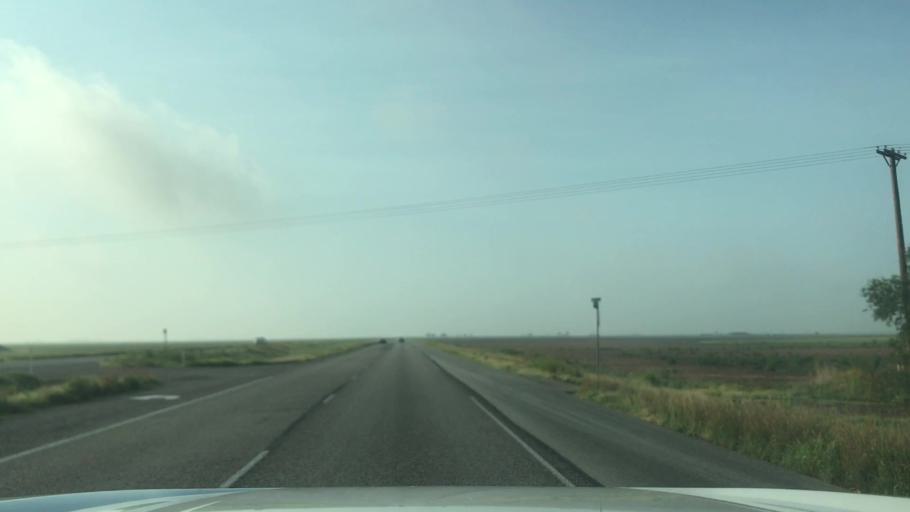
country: US
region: Texas
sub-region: Lubbock County
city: Slaton
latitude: 33.3455
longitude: -101.5454
